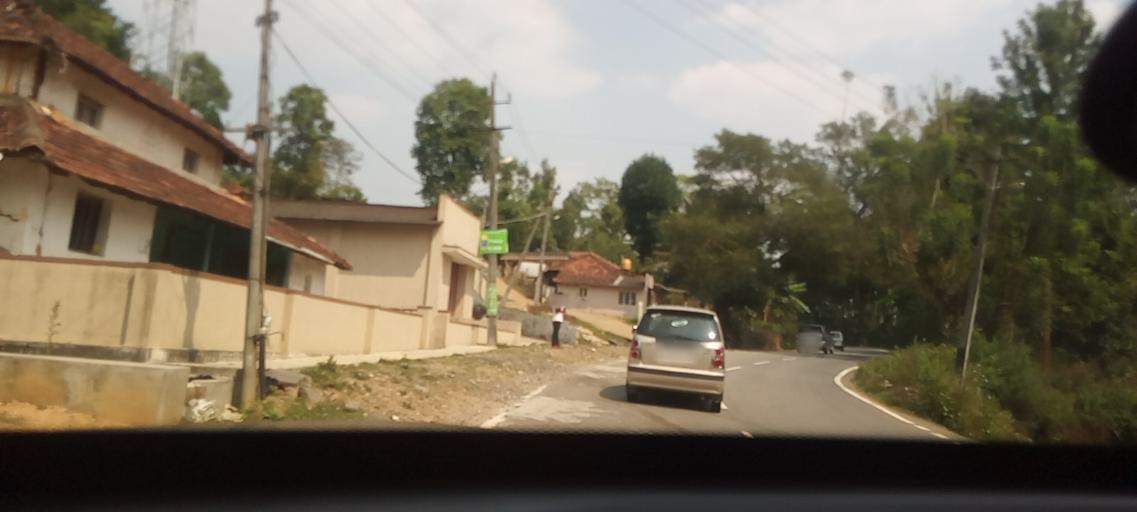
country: IN
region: Karnataka
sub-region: Chikmagalur
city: Chikmagalur
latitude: 13.2633
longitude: 75.6858
